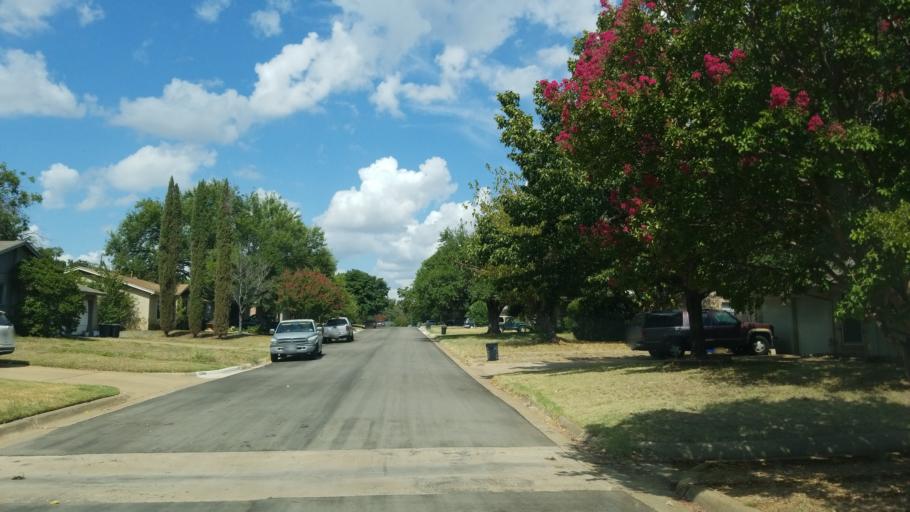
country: US
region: Texas
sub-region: Tarrant County
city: Euless
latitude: 32.8535
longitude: -97.0931
